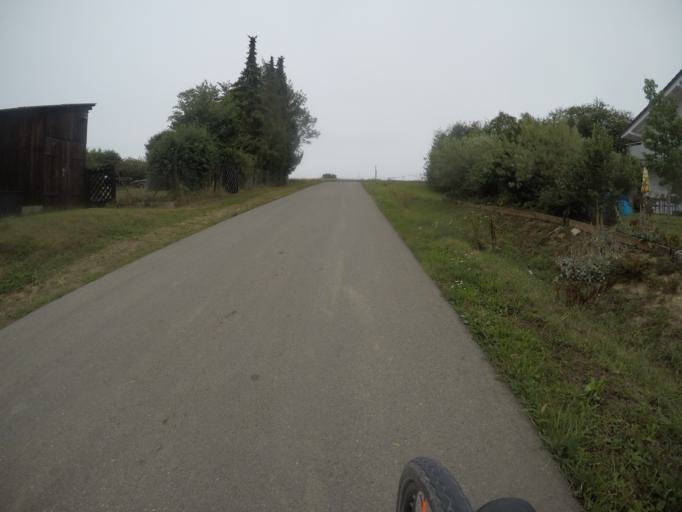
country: DE
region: Baden-Wuerttemberg
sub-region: Karlsruhe Region
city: Heimsheim
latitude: 48.8033
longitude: 8.8568
